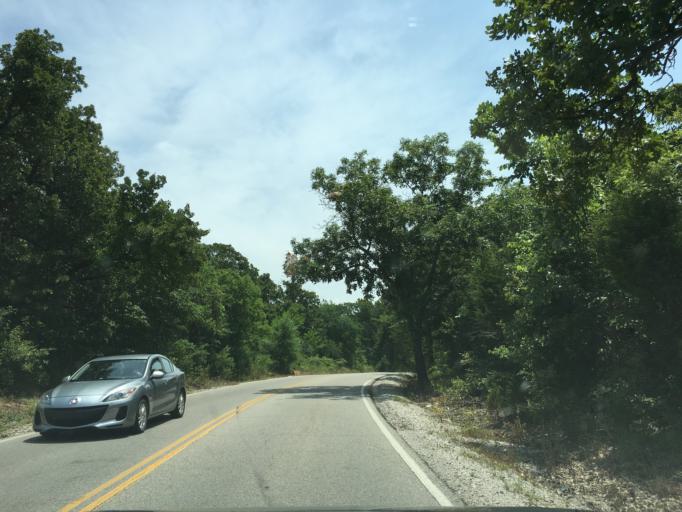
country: US
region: Oklahoma
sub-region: Tulsa County
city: Jenks
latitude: 36.0750
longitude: -96.0002
